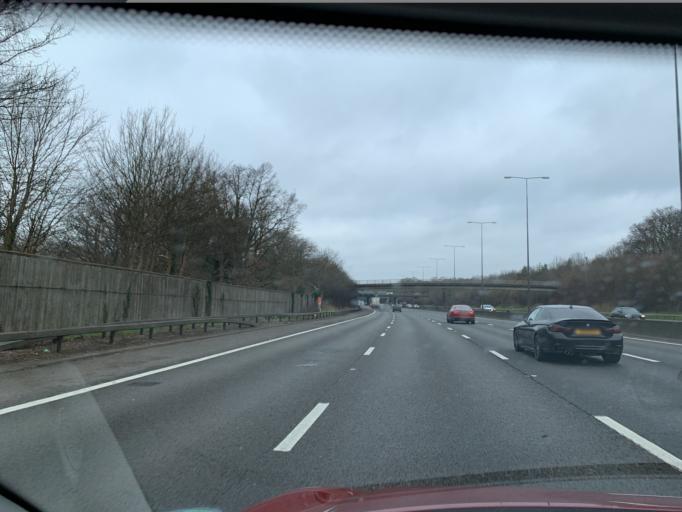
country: GB
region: England
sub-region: Surrey
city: Leatherhead
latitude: 51.3134
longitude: -0.3299
